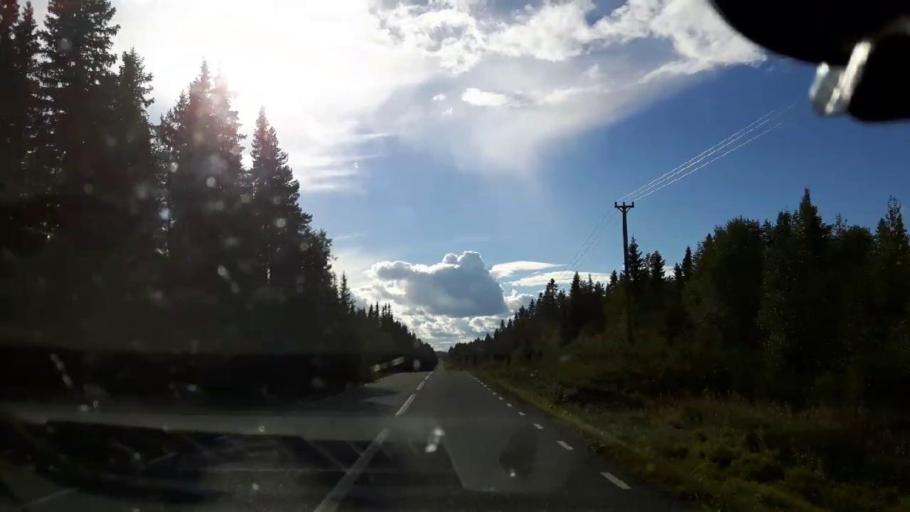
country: SE
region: Jaemtland
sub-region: Stroemsunds Kommun
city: Stroemsund
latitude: 63.5787
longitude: 15.6821
